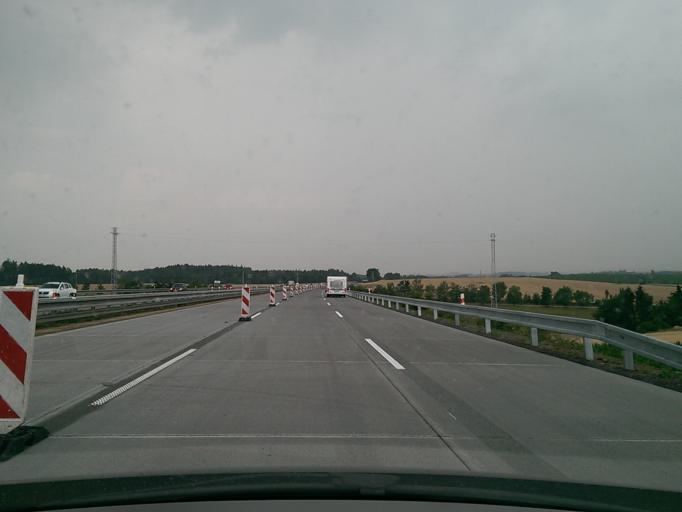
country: CZ
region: Vysocina
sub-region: Okres Zd'ar nad Sazavou
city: Velka Bites
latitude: 49.2786
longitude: 16.2110
